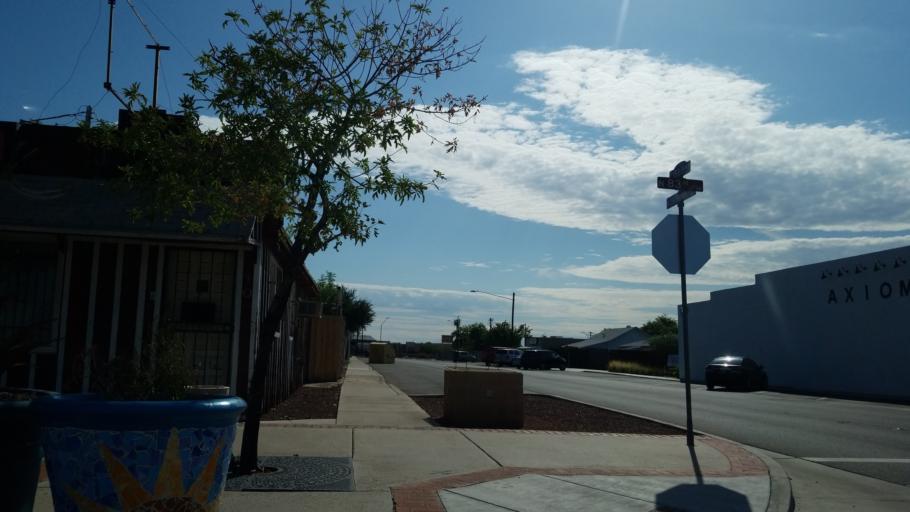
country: US
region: Arizona
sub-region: Maricopa County
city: Peoria
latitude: 33.5795
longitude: -112.2376
